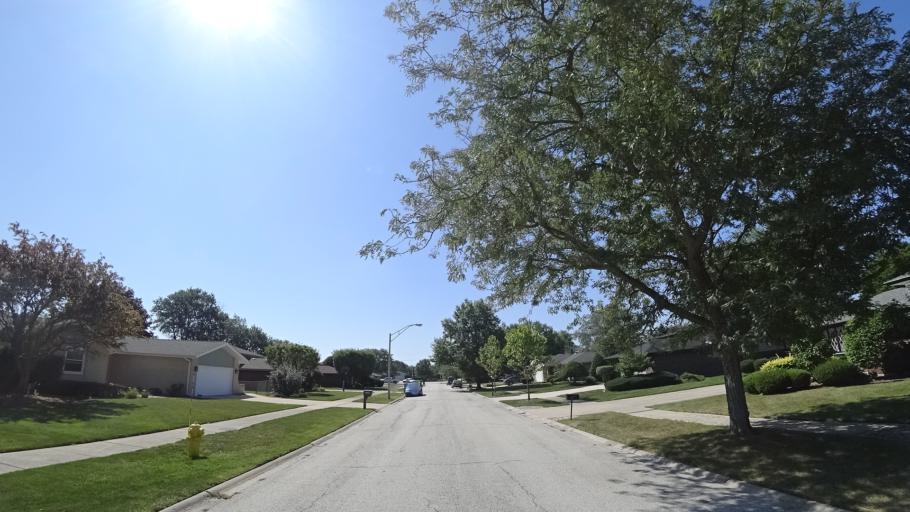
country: US
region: Illinois
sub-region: Cook County
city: Orland Park
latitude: 41.6329
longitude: -87.8254
